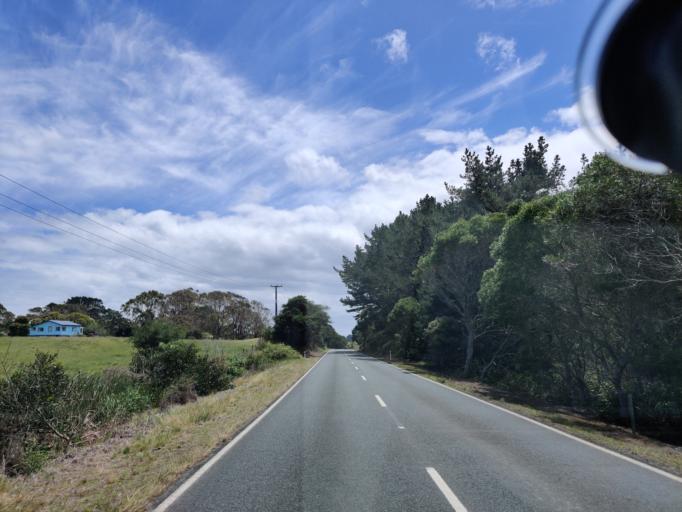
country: NZ
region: Northland
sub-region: Far North District
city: Kaitaia
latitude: -34.7406
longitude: 173.0462
